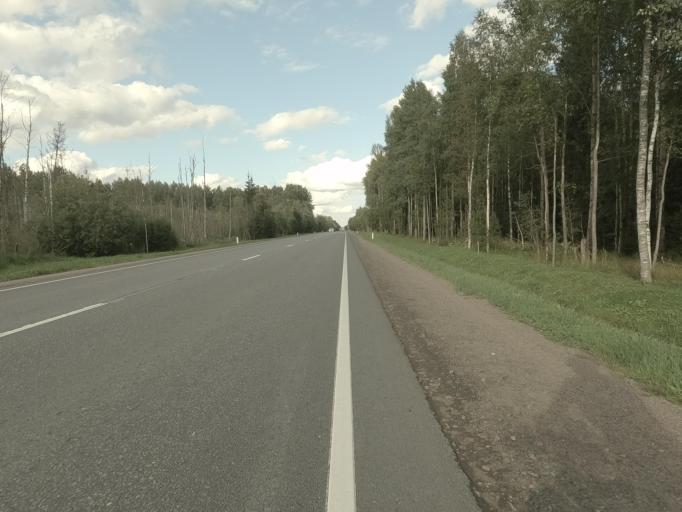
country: RU
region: Leningrad
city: Mga
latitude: 59.6837
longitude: 30.9569
